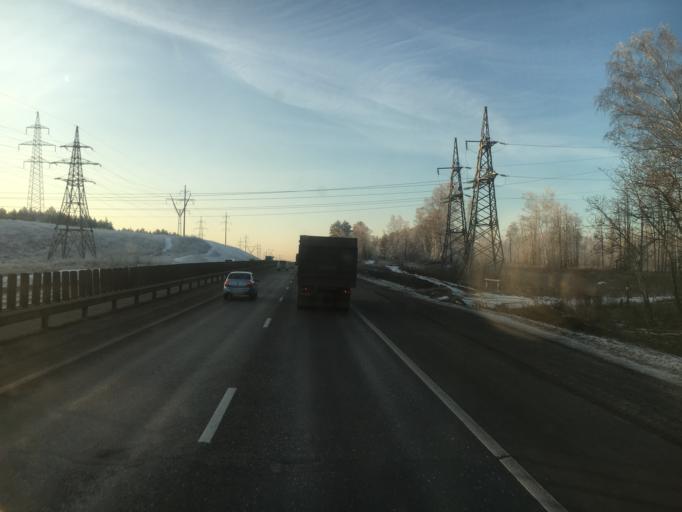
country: RU
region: Samara
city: Pribrezhnyy
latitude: 53.5134
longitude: 49.9101
